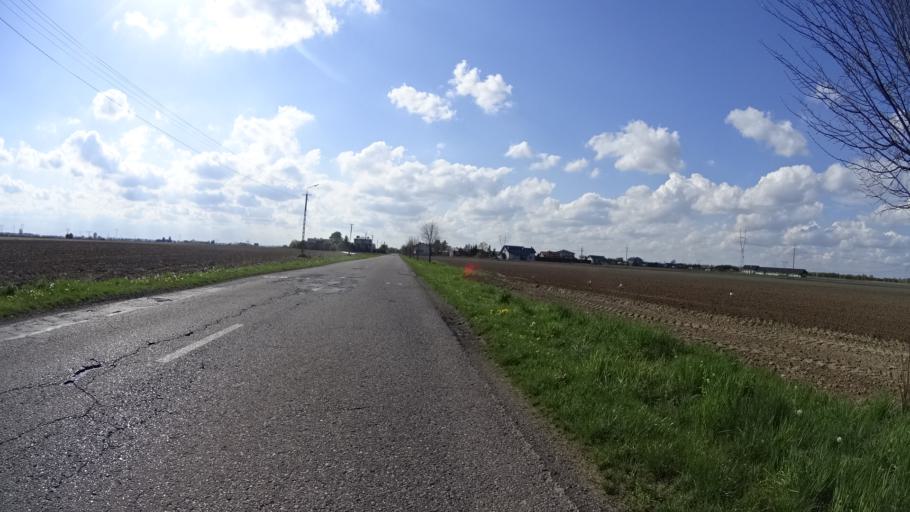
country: PL
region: Masovian Voivodeship
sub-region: Powiat warszawski zachodni
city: Jozefow
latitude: 52.2335
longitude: 20.6810
